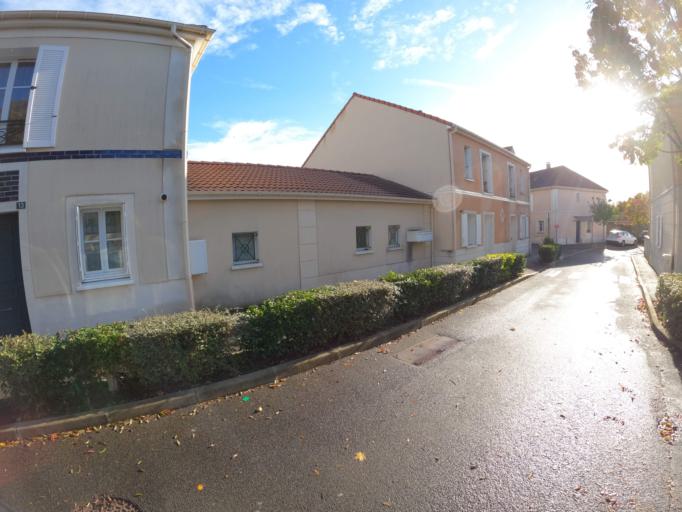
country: FR
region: Ile-de-France
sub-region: Departement de Seine-et-Marne
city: Bailly-Romainvilliers
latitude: 48.8500
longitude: 2.8209
